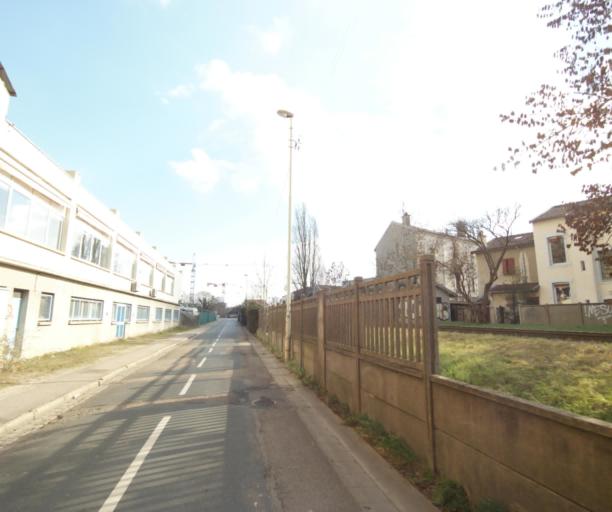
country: FR
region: Lorraine
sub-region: Departement de Meurthe-et-Moselle
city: Malzeville
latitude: 48.7001
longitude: 6.1923
